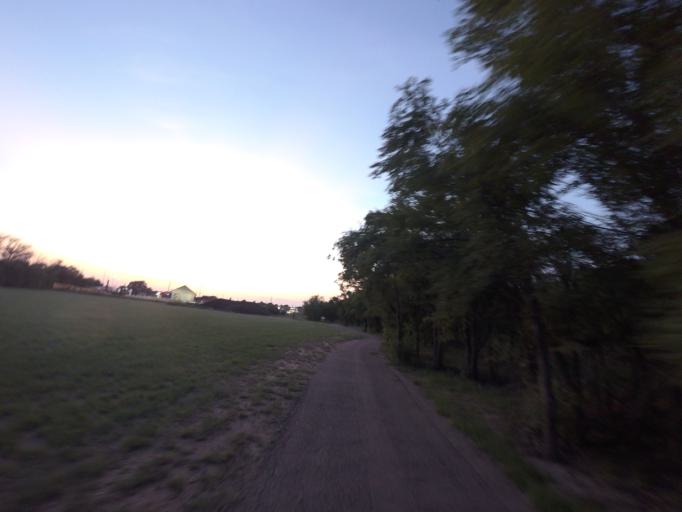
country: US
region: New Mexico
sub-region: Curry County
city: Clovis
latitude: 34.4300
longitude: -103.1938
